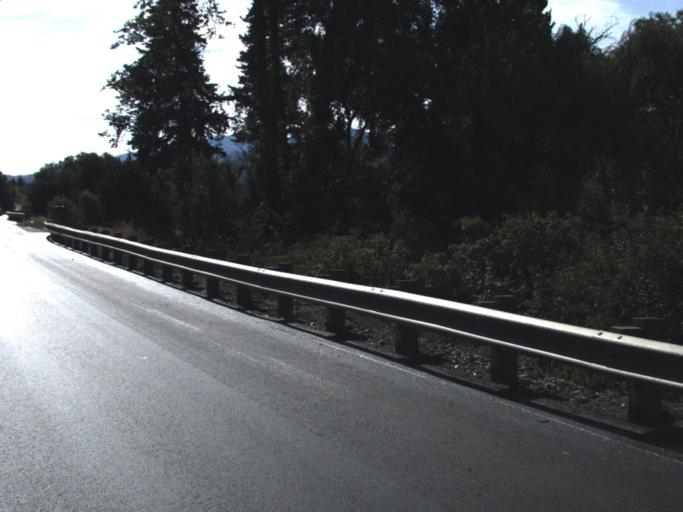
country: US
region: Washington
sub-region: Stevens County
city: Colville
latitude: 48.5273
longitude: -117.9027
